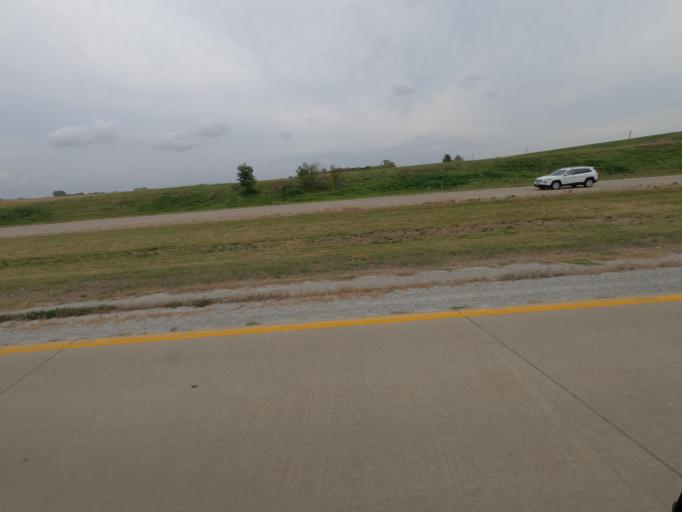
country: US
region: Iowa
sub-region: Jasper County
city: Monroe
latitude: 41.5234
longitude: -93.1304
